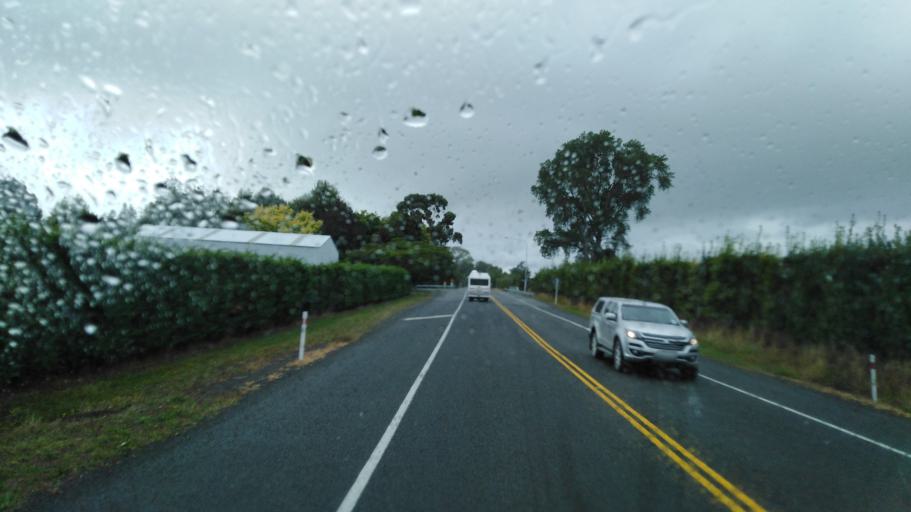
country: NZ
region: Marlborough
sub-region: Marlborough District
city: Blenheim
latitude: -41.4591
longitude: 173.9467
